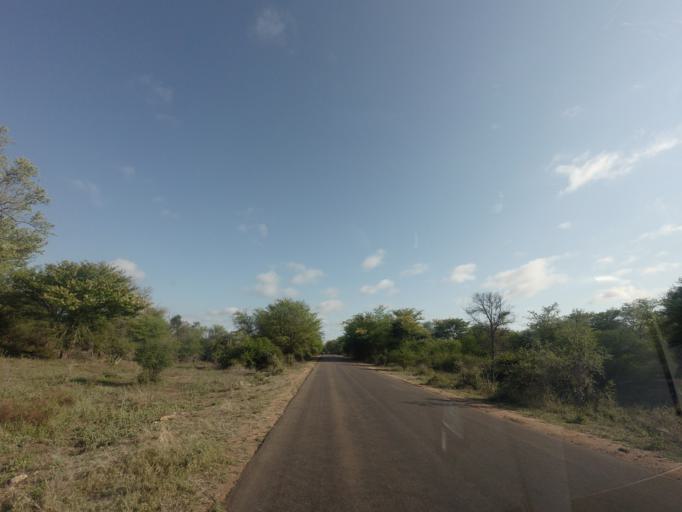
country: ZA
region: Mpumalanga
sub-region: Ehlanzeni District
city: Komatipoort
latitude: -25.2700
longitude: 31.8483
